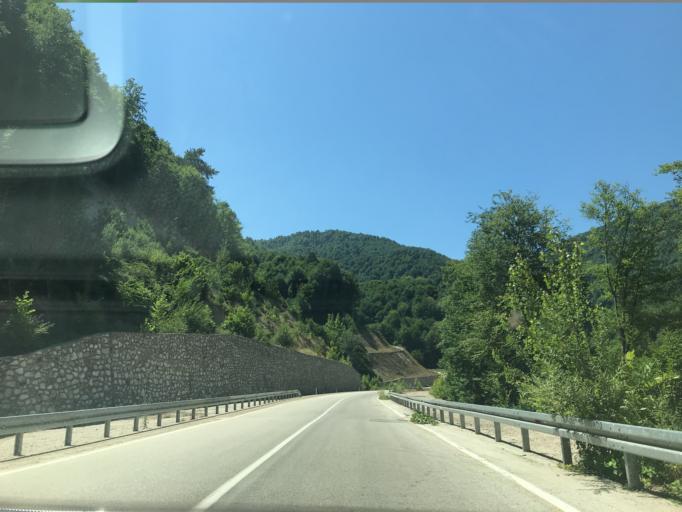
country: TR
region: Bursa
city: Tahtakopru
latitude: 39.9345
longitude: 29.5892
